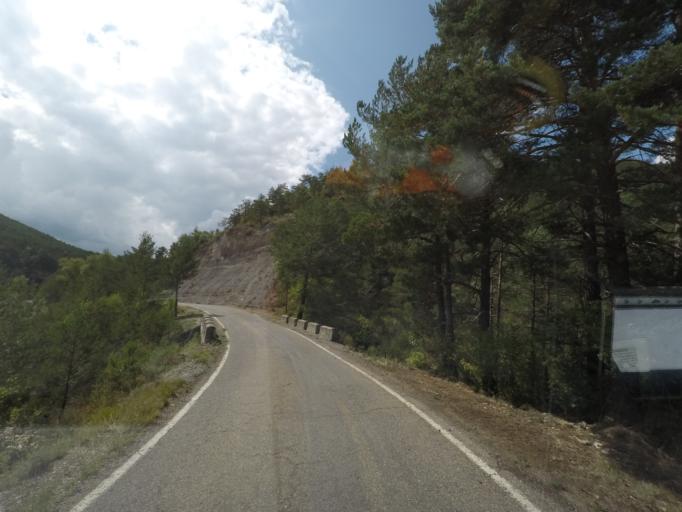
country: ES
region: Aragon
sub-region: Provincia de Huesca
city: Yebra de Basa
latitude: 42.4095
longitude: -0.2230
